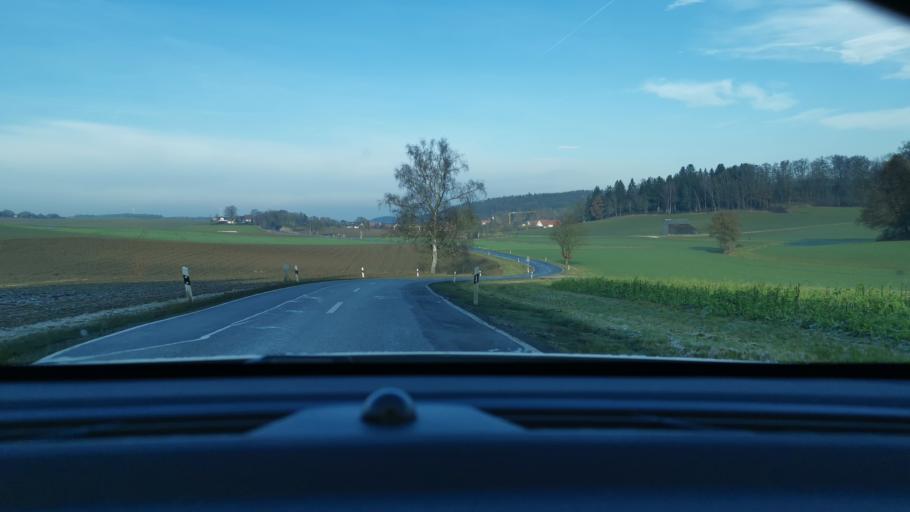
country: DE
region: Bavaria
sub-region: Swabia
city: Petersdorf
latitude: 48.5498
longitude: 10.9965
